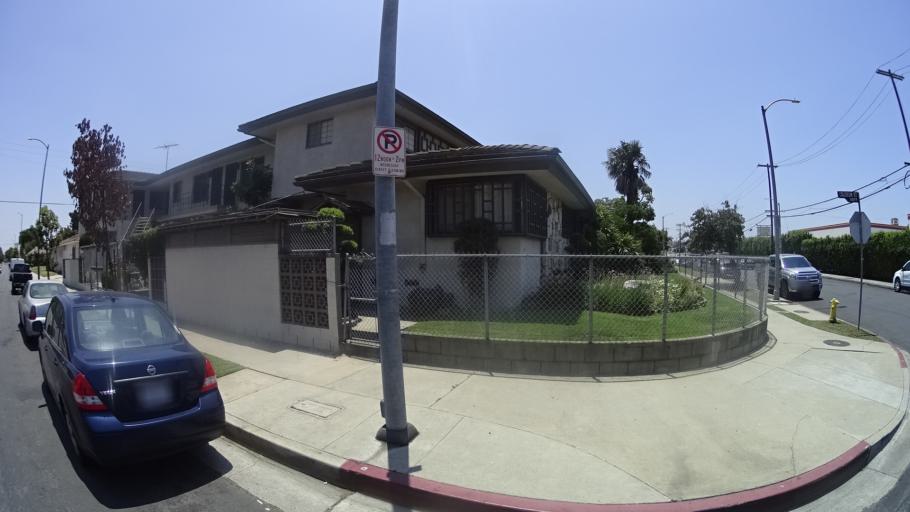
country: US
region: California
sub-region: Los Angeles County
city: View Park-Windsor Hills
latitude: 34.0182
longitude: -118.3338
